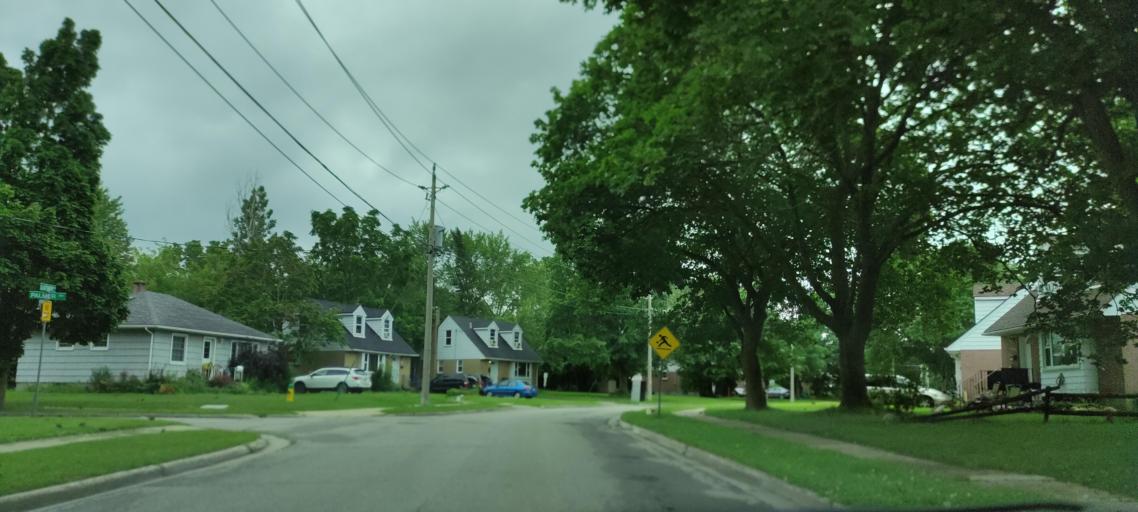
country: CA
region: Ontario
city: Stratford
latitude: 43.3807
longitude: -80.9811
